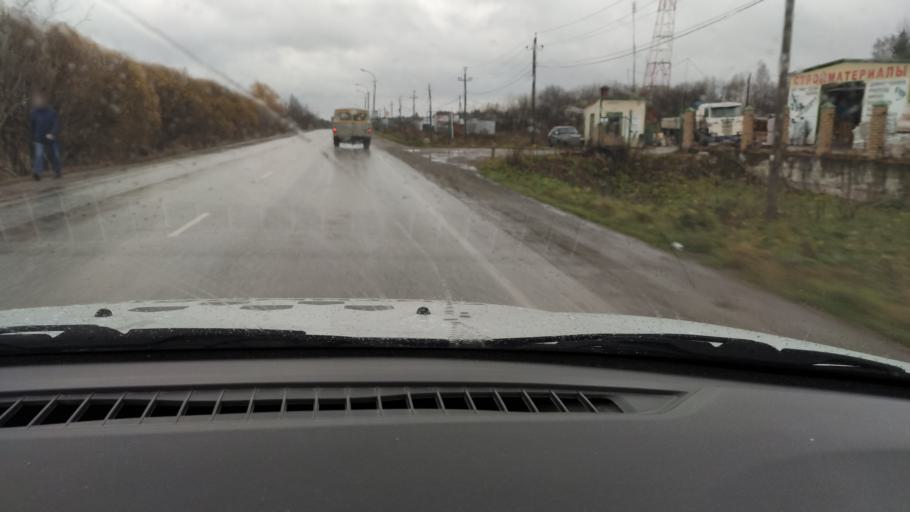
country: RU
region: Perm
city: Sylva
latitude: 58.0266
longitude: 56.7298
